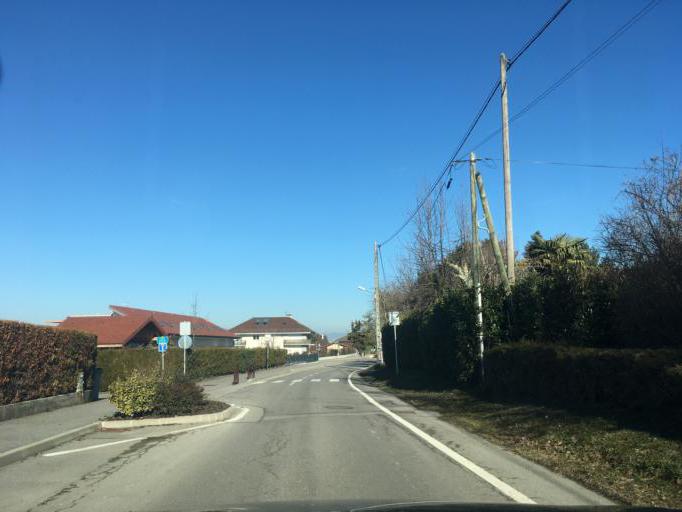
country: FR
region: Rhone-Alpes
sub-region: Departement de la Haute-Savoie
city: Cranves-Sales
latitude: 46.1898
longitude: 6.2908
